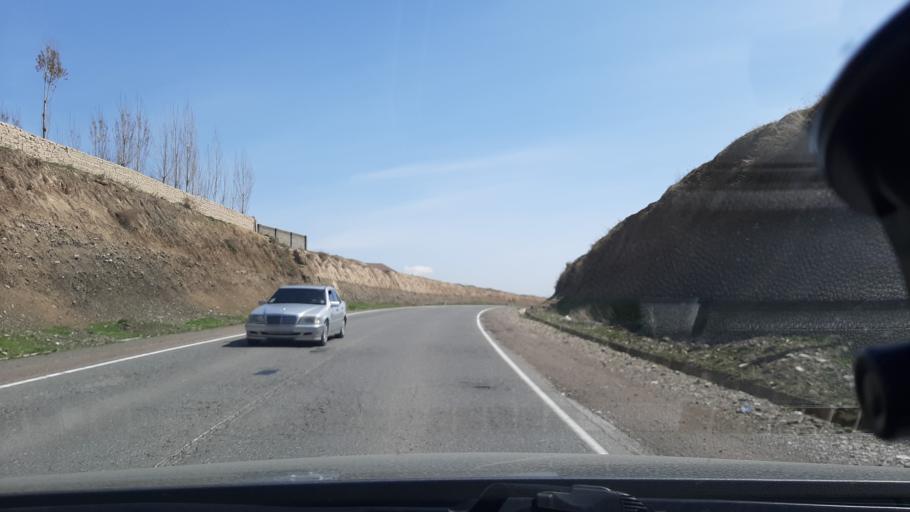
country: TJ
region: Viloyati Sughd
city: Shahriston
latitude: 39.7622
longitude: 68.8025
